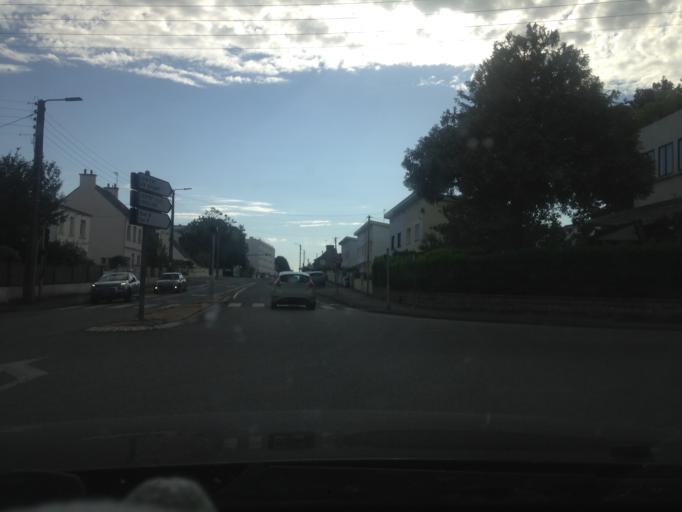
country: FR
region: Brittany
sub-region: Departement du Morbihan
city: Lanester
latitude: 47.7623
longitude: -3.3371
